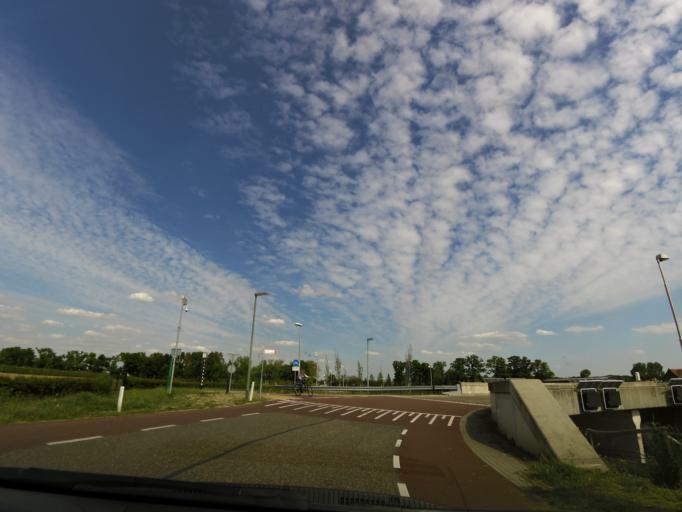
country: NL
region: Limburg
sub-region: Gemeente Roermond
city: Roermond
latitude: 51.1749
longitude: 5.9831
